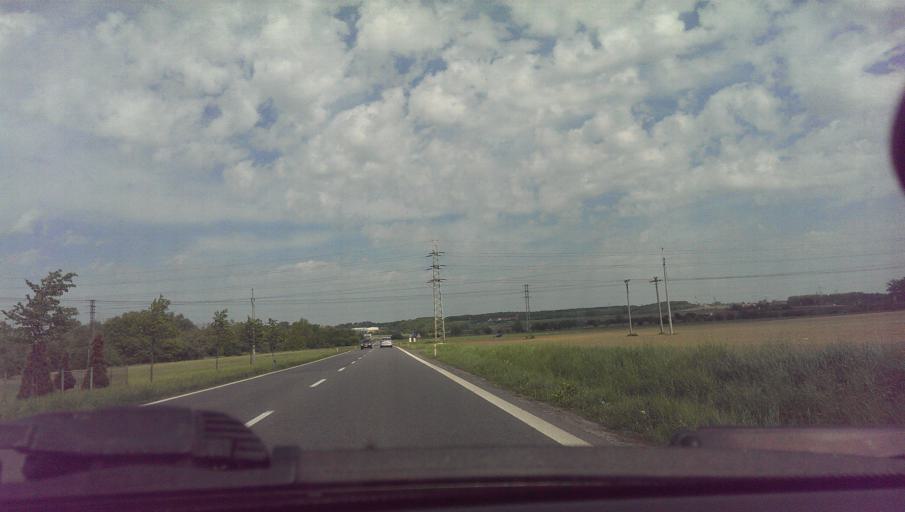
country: CZ
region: Zlin
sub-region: Okres Zlin
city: Otrokovice
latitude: 49.2154
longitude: 17.5291
